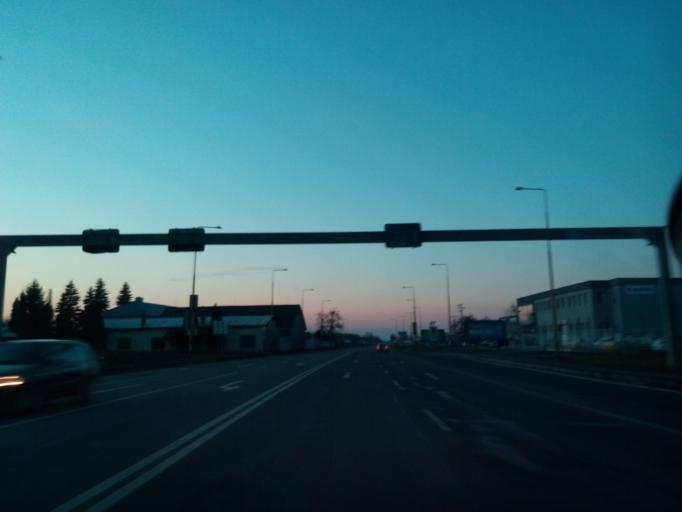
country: SK
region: Kosicky
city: Michalovce
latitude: 48.7533
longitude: 21.8987
